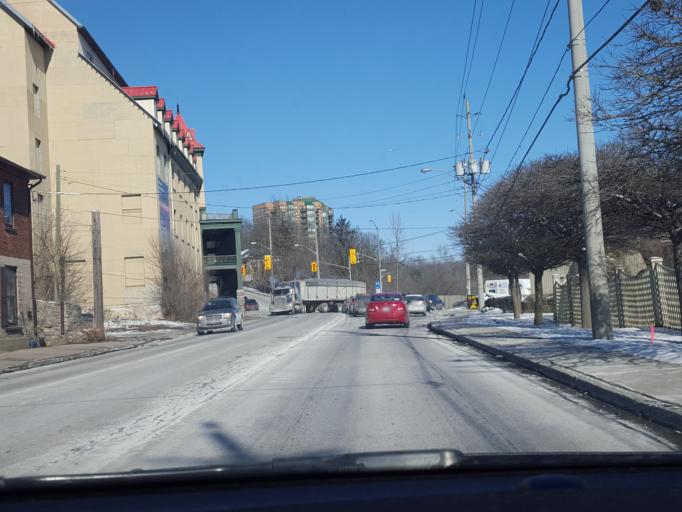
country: CA
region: Ontario
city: Cambridge
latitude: 43.3991
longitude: -80.3701
